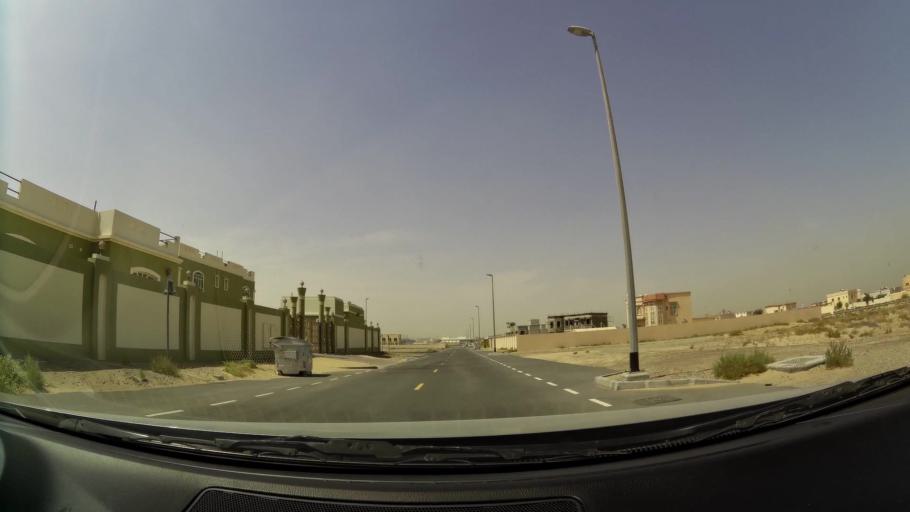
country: AE
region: Ash Shariqah
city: Sharjah
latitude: 25.1881
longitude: 55.4298
